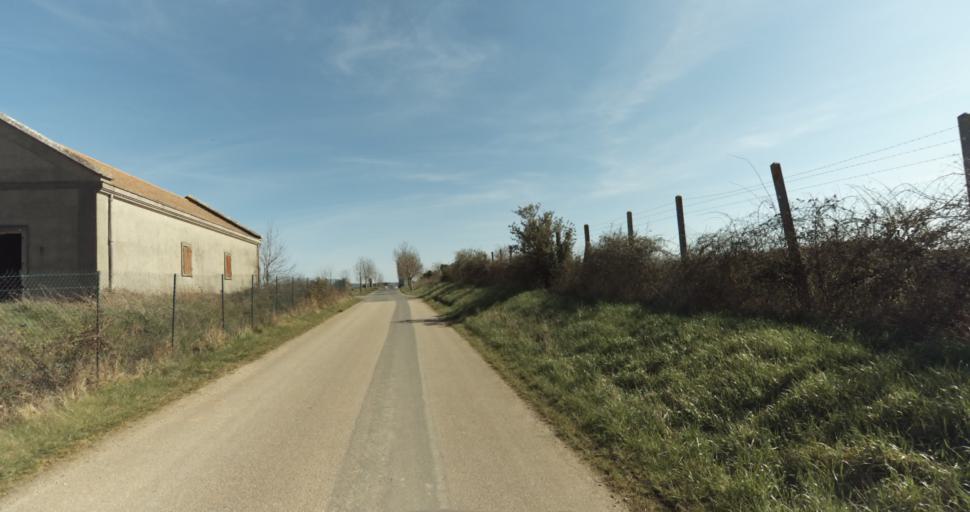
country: FR
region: Lower Normandy
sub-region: Departement du Calvados
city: Saint-Pierre-sur-Dives
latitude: 49.0467
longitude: -0.0477
